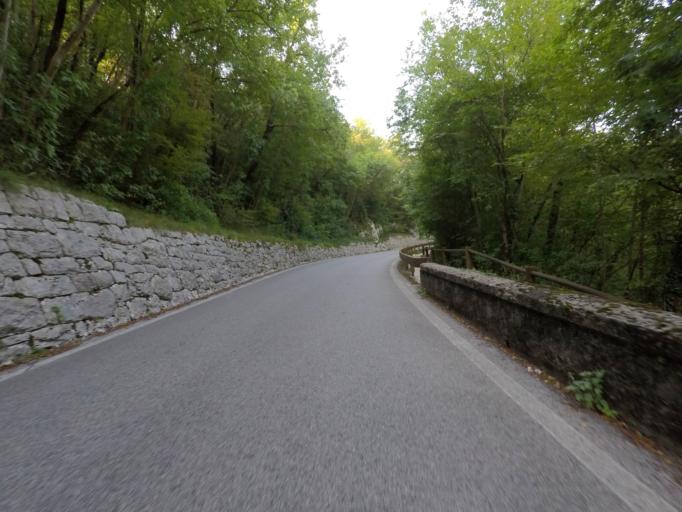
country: IT
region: Friuli Venezia Giulia
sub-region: Provincia di Udine
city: Forgaria nel Friuli
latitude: 46.2287
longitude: 13.0249
